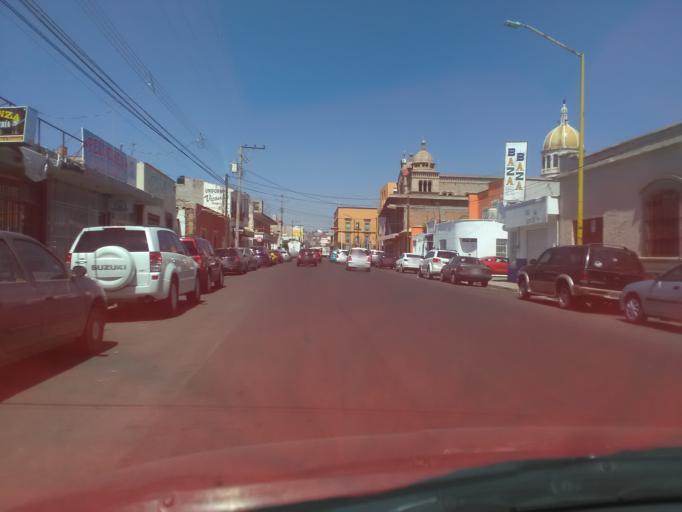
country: MX
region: Durango
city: Victoria de Durango
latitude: 24.0250
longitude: -104.6599
